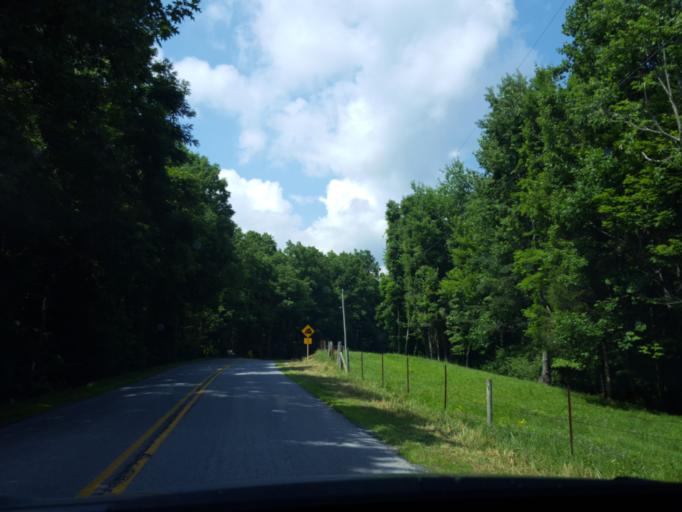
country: US
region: Virginia
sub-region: Nelson County
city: Nellysford
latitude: 37.9091
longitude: -78.9894
